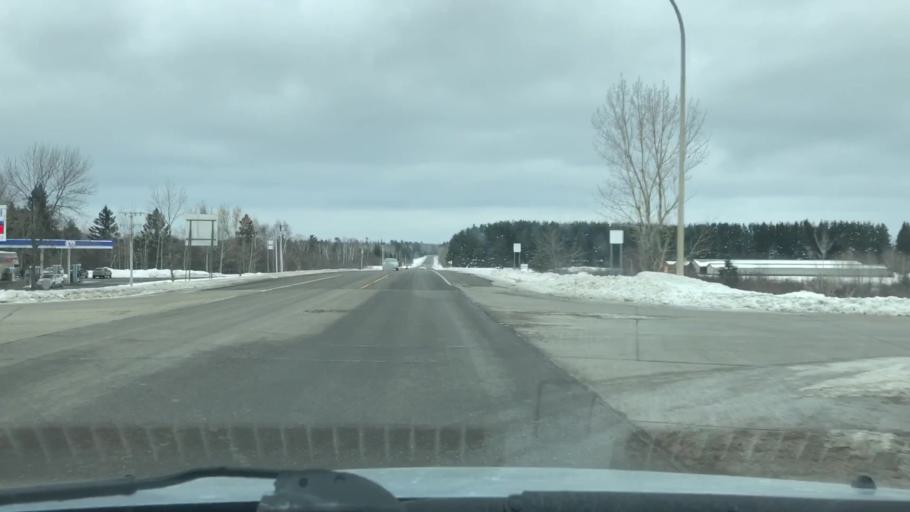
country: US
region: Minnesota
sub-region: Carlton County
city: Esko
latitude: 46.6955
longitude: -92.3651
